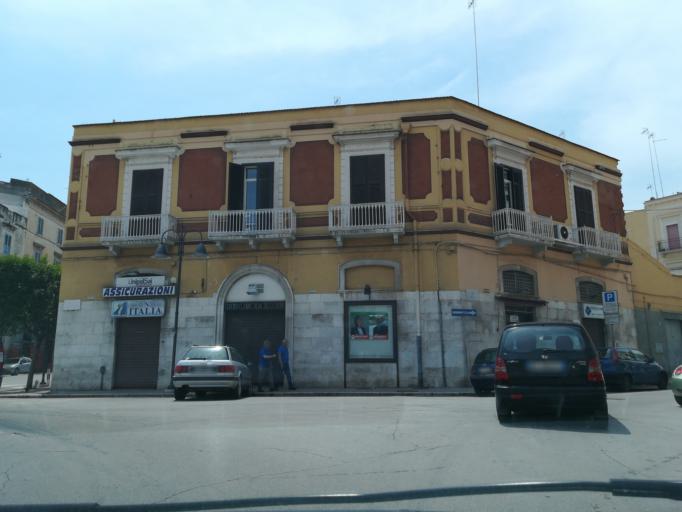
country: IT
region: Apulia
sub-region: Provincia di Barletta - Andria - Trani
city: Barletta
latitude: 41.3186
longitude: 16.2784
